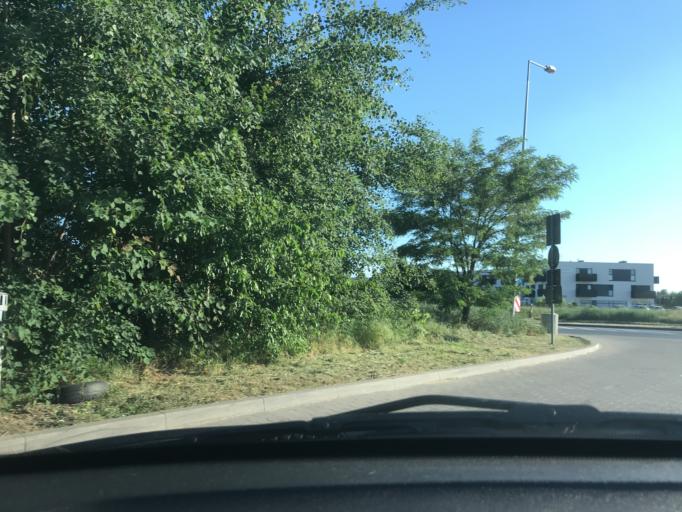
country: PL
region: Greater Poland Voivodeship
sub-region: Powiat poznanski
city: Plewiska
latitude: 52.4119
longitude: 16.8329
